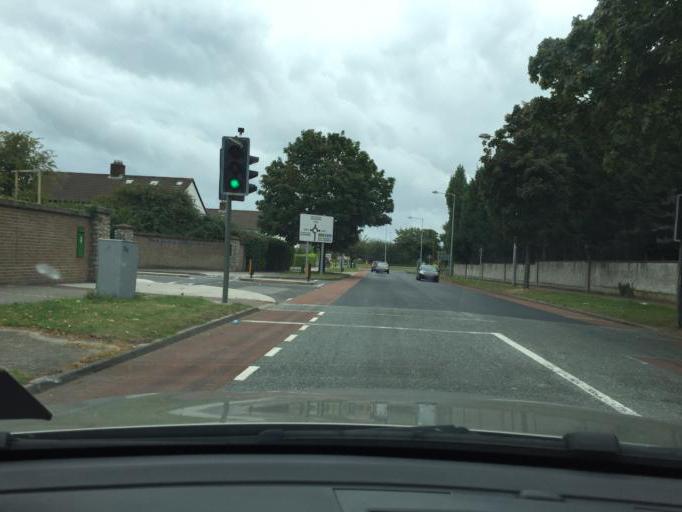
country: IE
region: Leinster
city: Templeogue
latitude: 53.3033
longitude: -6.3112
